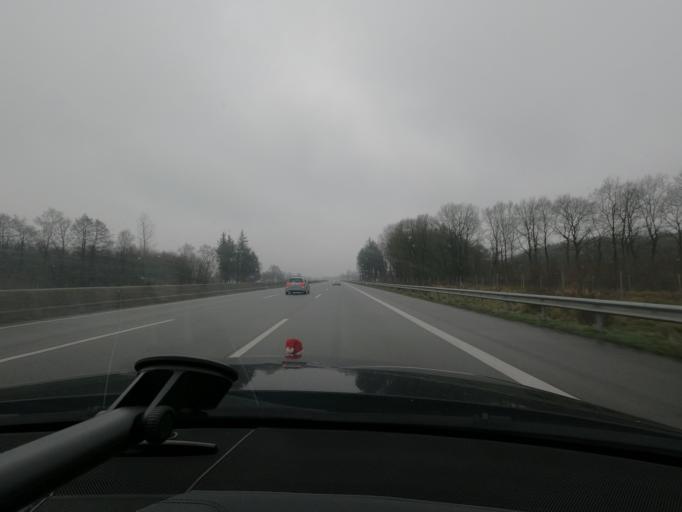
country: DE
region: Schleswig-Holstein
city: Bimohlen
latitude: 53.9262
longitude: 9.9407
